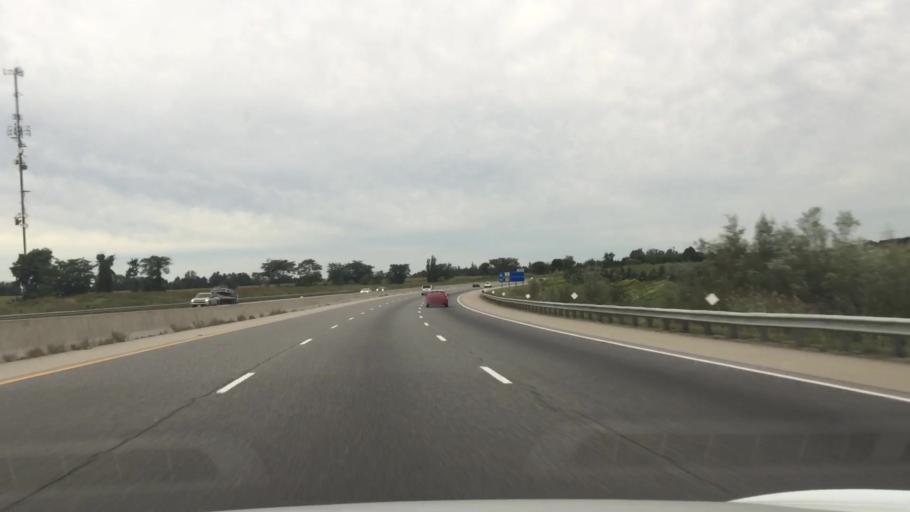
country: CA
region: Ontario
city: Kitchener
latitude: 43.2414
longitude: -80.5752
